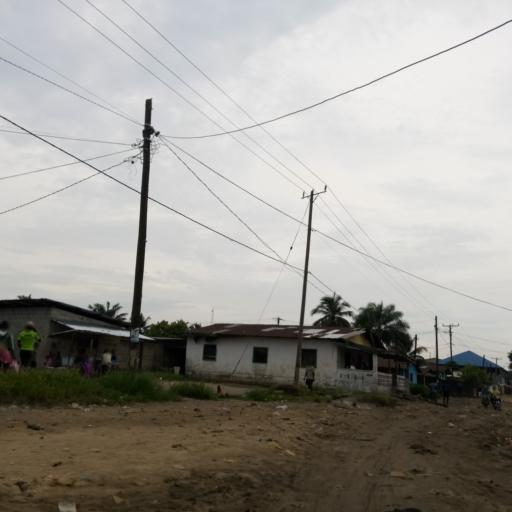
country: LR
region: Montserrado
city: Monrovia
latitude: 6.2936
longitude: -10.6842
